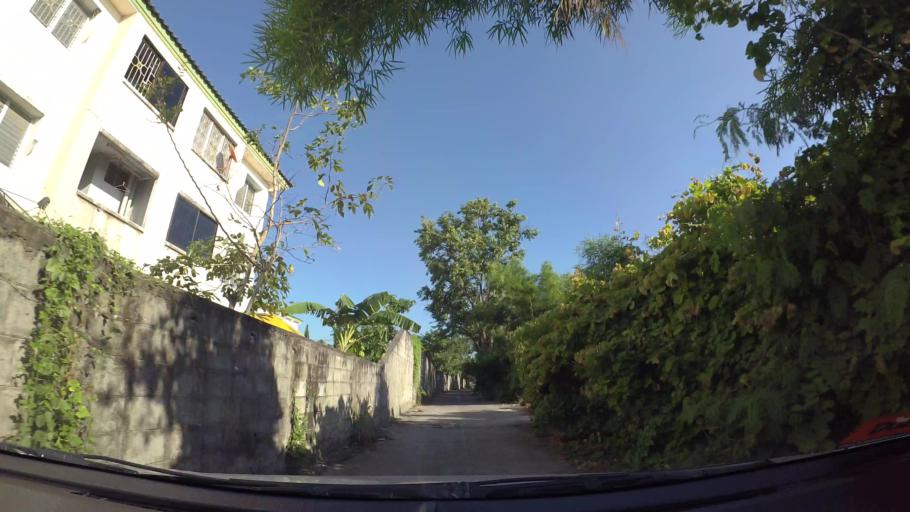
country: TH
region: Chon Buri
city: Si Racha
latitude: 13.1465
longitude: 100.9377
